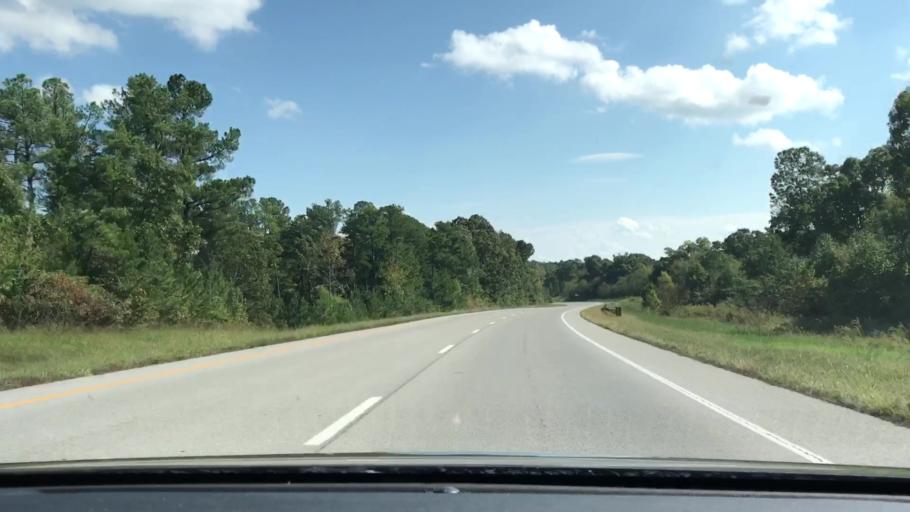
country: US
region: Kentucky
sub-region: Trigg County
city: Cadiz
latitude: 36.7815
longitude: -88.0486
